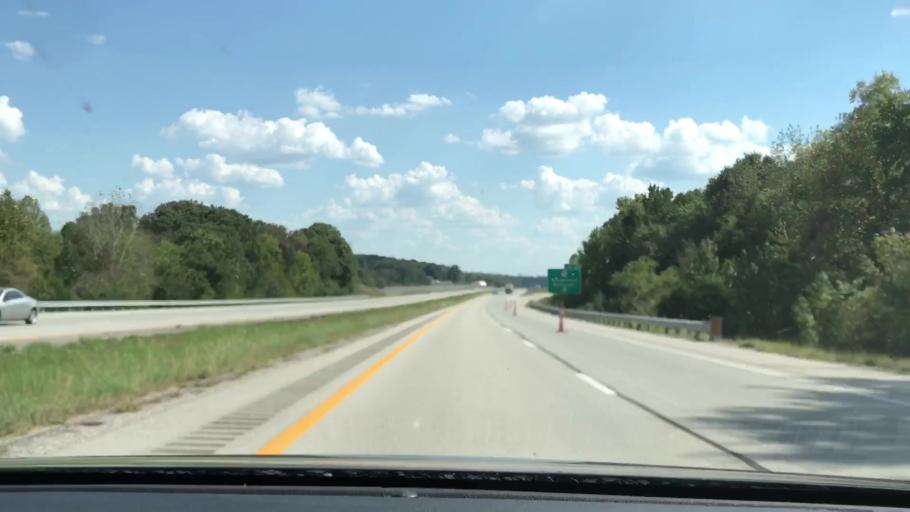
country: US
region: Kentucky
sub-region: Butler County
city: Morgantown
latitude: 37.2199
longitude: -86.7148
